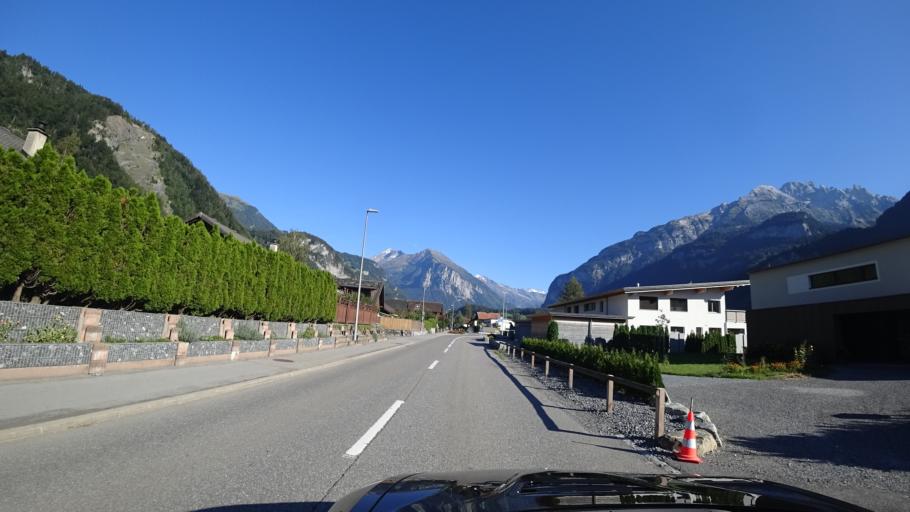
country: CH
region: Bern
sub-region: Interlaken-Oberhasli District
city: Meiringen
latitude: 46.7312
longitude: 8.1775
